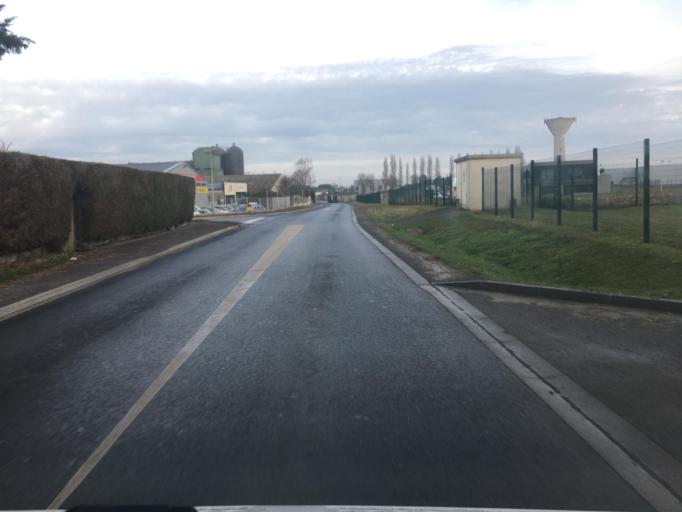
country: FR
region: Lower Normandy
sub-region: Departement du Calvados
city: Creully
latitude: 49.2743
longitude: -0.5464
